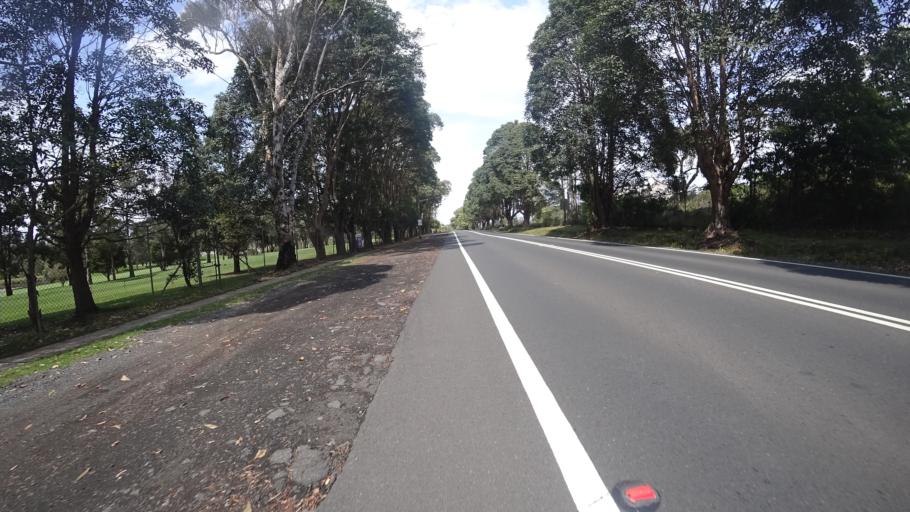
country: AU
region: New South Wales
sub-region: Hornsby Shire
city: Mount Colah
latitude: -33.6808
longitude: 151.1121
